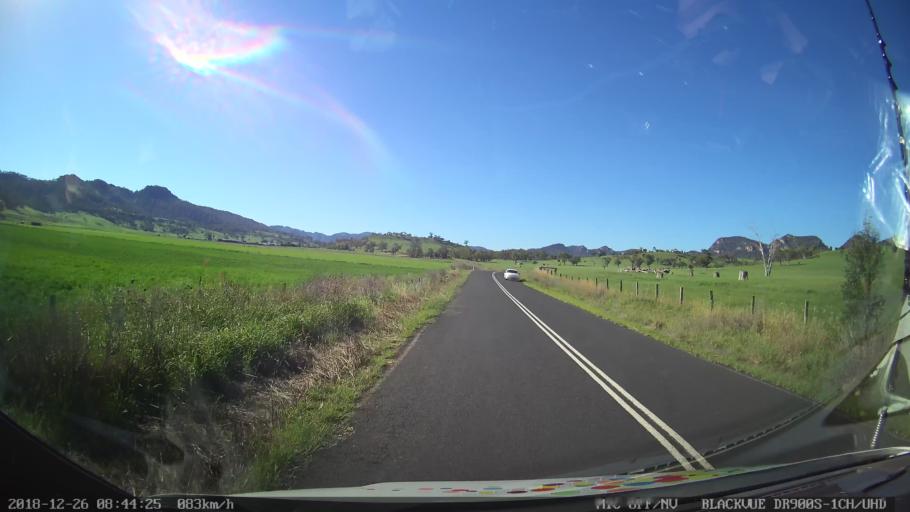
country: AU
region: New South Wales
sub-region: Mid-Western Regional
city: Kandos
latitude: -32.5144
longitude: 150.0809
